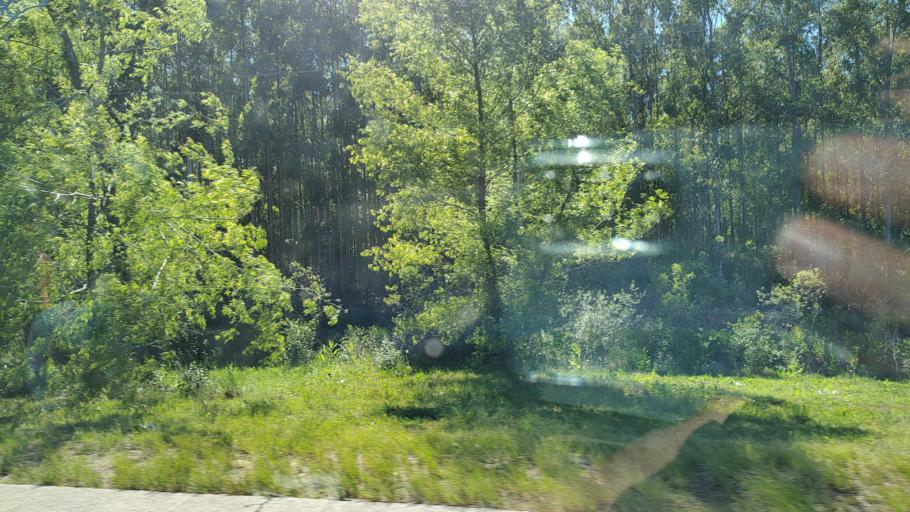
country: AR
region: Entre Rios
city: Ubajay
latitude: -31.8834
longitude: -58.3251
